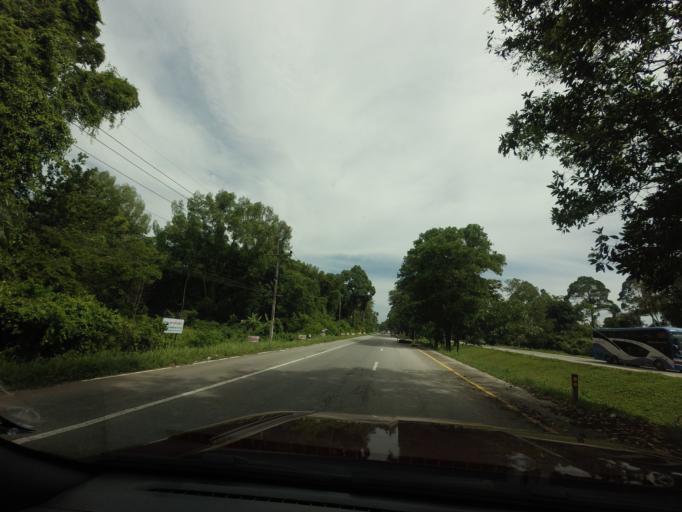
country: TH
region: Narathiwat
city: Tak Bai
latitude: 6.2729
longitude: 102.0242
